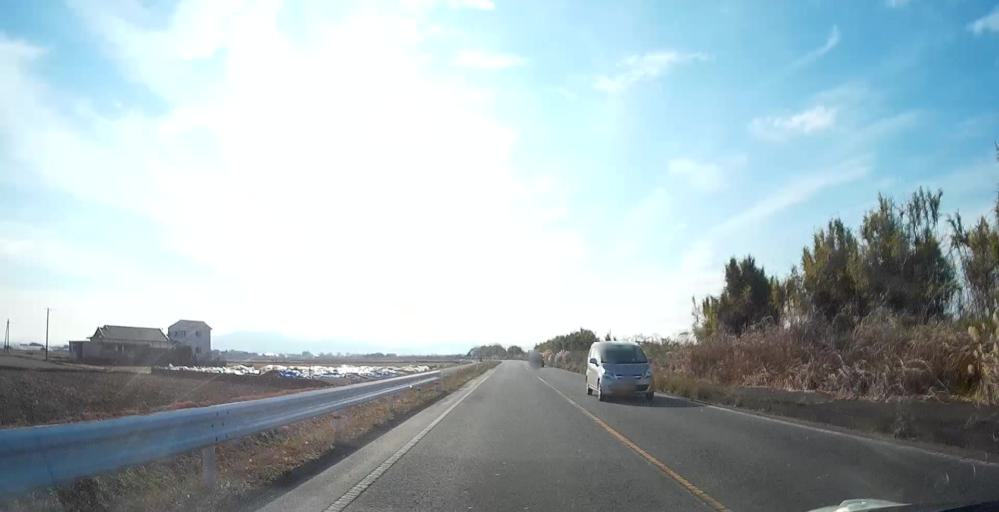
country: JP
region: Kumamoto
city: Uto
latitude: 32.7403
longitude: 130.6688
